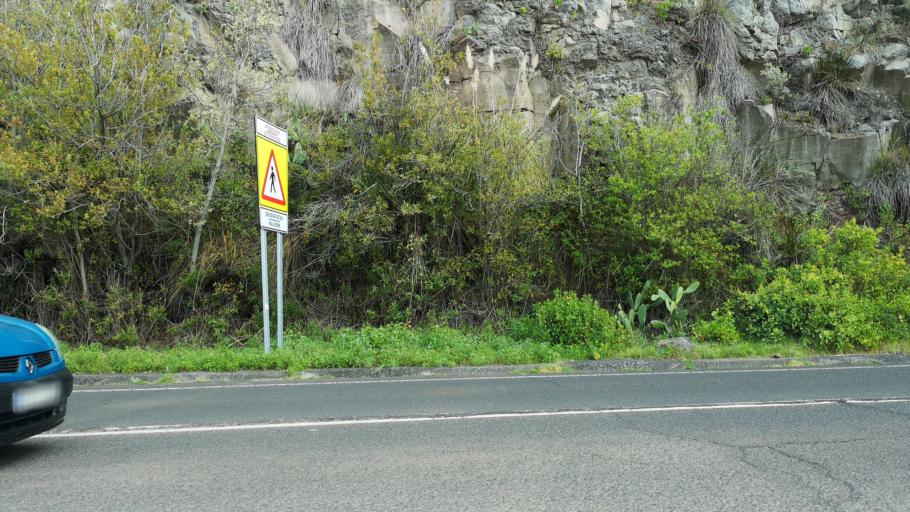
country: ES
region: Canary Islands
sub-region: Provincia de Santa Cruz de Tenerife
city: Vallehermosa
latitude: 28.1268
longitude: -17.3219
